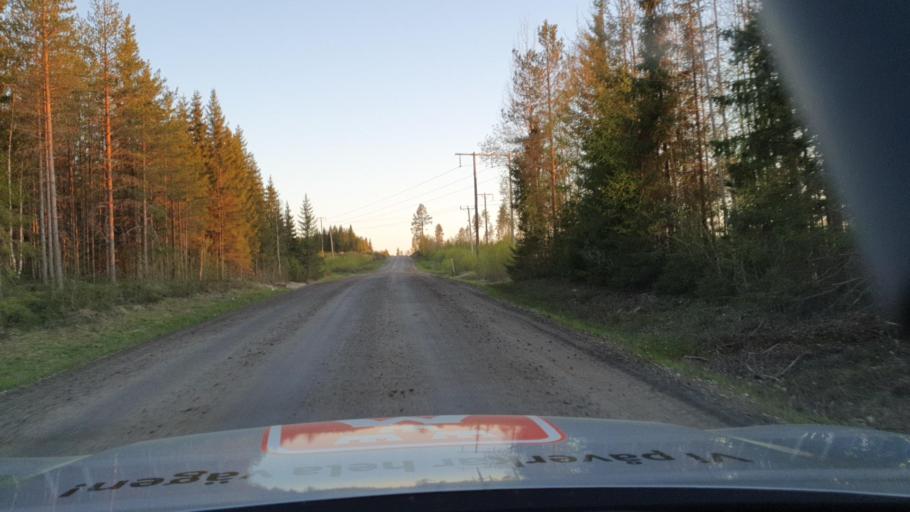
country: SE
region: Vaesternorrland
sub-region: OErnskoeldsviks Kommun
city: Ornskoldsvik
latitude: 63.5184
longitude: 18.5061
